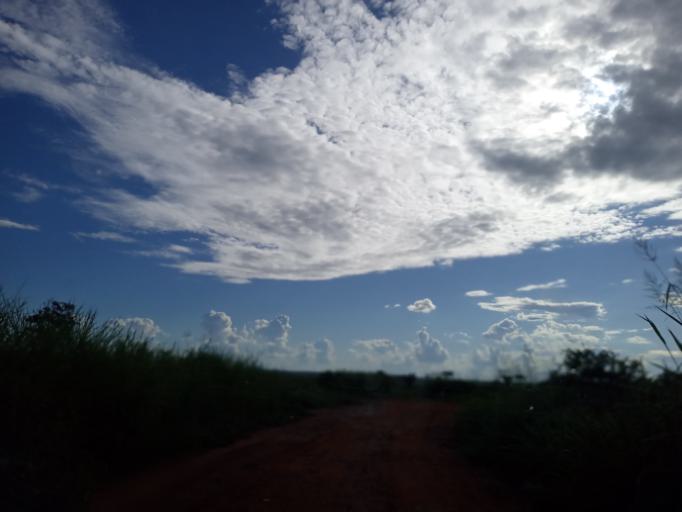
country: BR
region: Minas Gerais
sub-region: Ituiutaba
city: Ituiutaba
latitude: -18.9617
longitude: -49.4993
